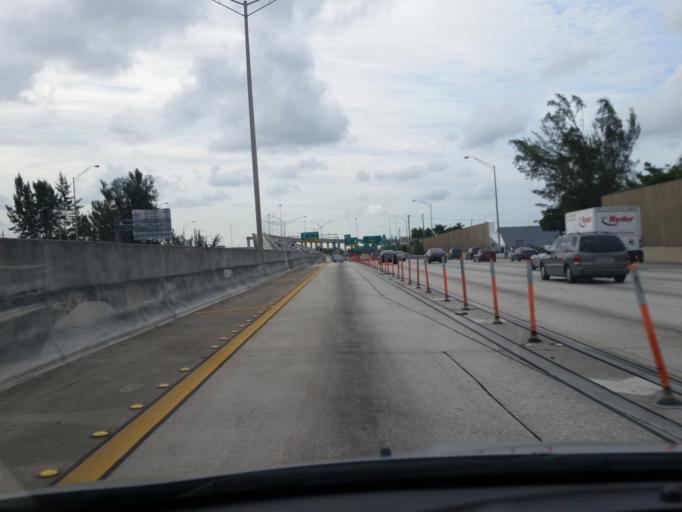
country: US
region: Florida
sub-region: Miami-Dade County
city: Golden Glades
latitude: 25.9160
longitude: -80.2102
